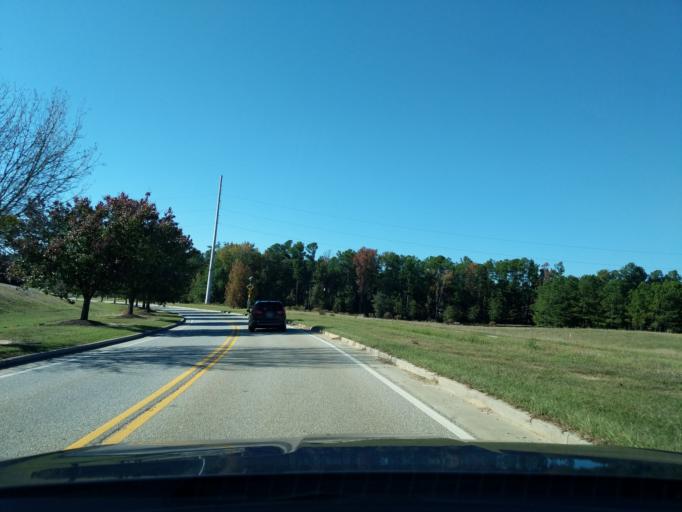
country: US
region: Georgia
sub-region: Columbia County
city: Grovetown
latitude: 33.4657
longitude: -82.1841
